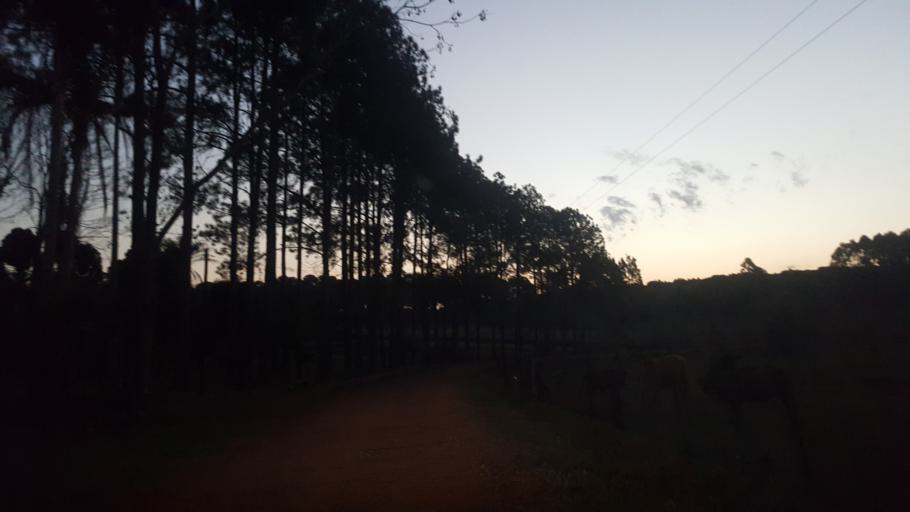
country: AR
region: Misiones
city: Capiovi
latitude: -26.9029
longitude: -55.0526
